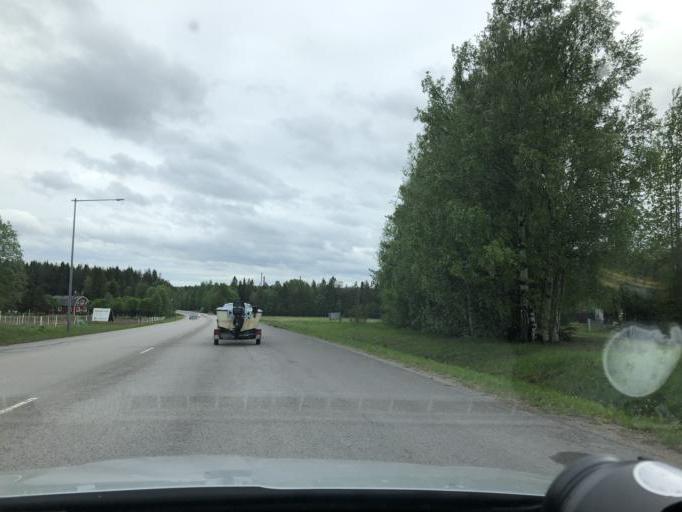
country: SE
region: Norrbotten
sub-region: Pitea Kommun
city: Pitea
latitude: 65.2862
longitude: 21.5072
